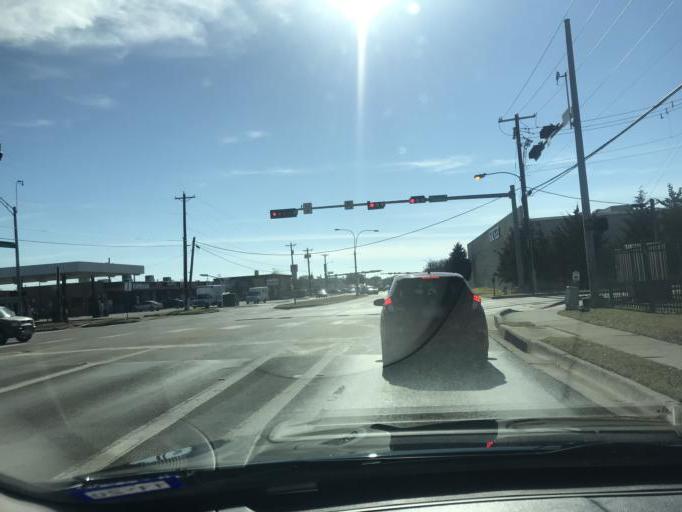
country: US
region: Texas
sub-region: Denton County
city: Denton
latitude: 33.2327
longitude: -97.1370
